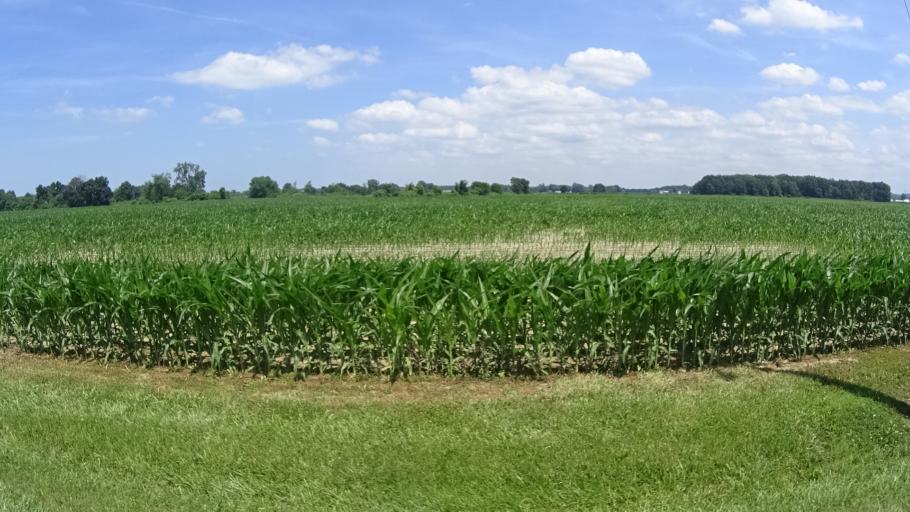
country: US
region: Ohio
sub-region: Erie County
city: Huron
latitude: 41.3629
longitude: -82.5389
